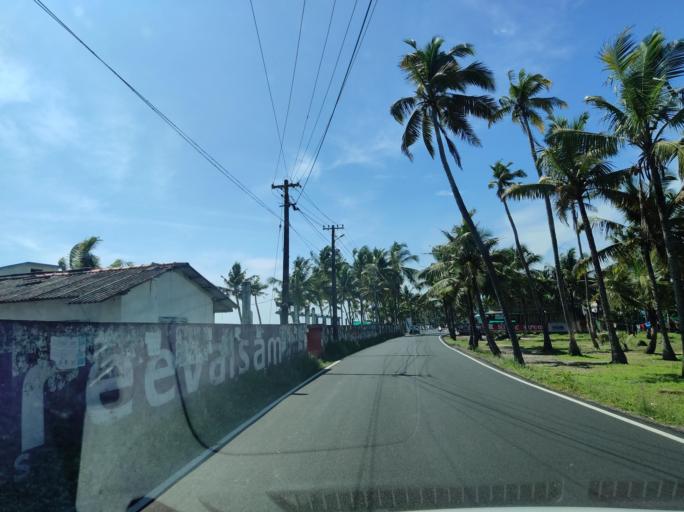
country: IN
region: Kerala
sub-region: Alappuzha
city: Kayankulam
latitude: 9.2469
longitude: 76.4126
